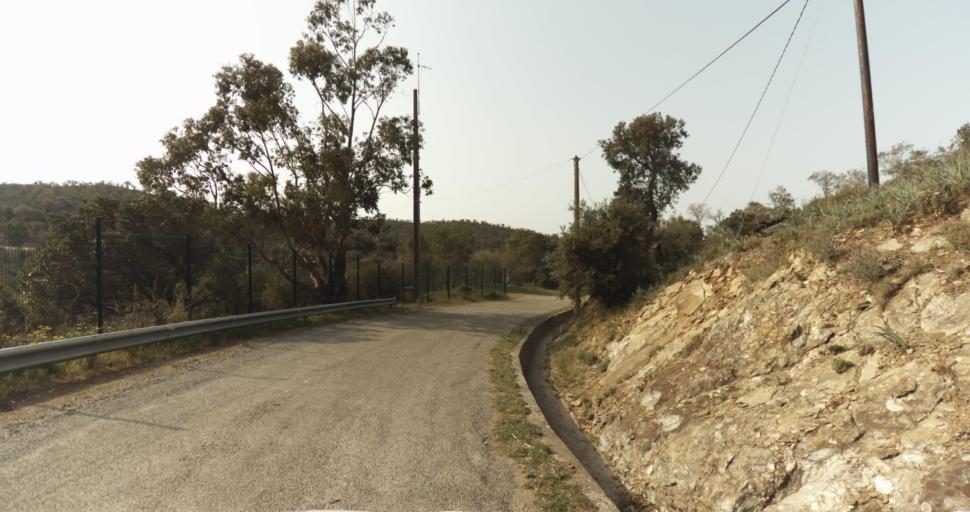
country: FR
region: Provence-Alpes-Cote d'Azur
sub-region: Departement du Var
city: Bormes-les-Mimosas
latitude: 43.1406
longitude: 6.2896
